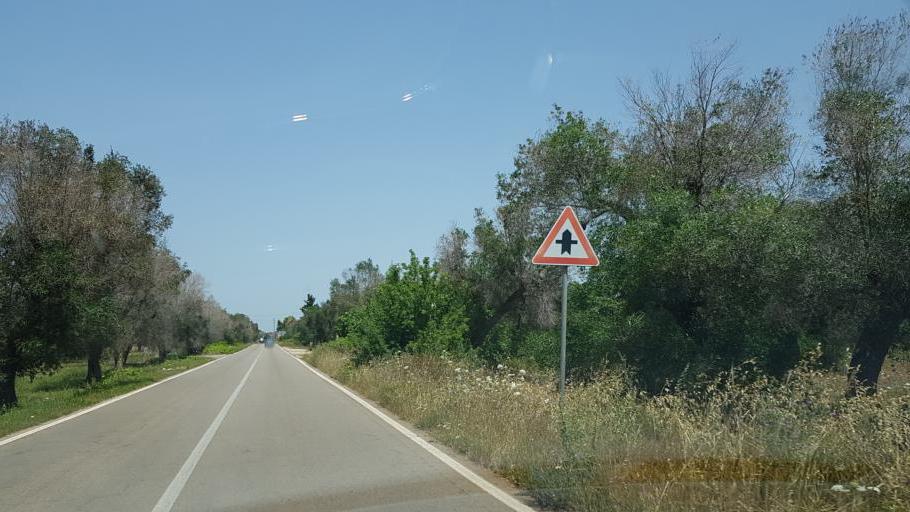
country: IT
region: Apulia
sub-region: Provincia di Lecce
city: Veglie
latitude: 40.3226
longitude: 17.9244
